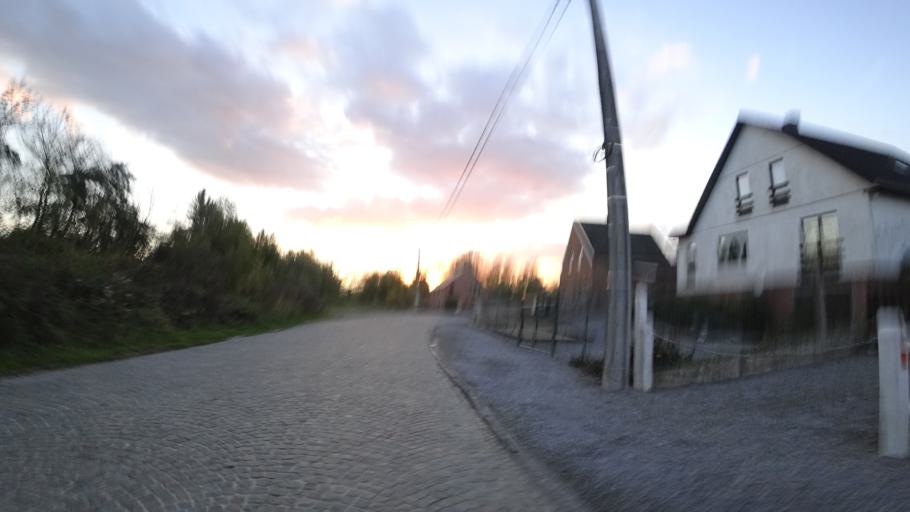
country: BE
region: Wallonia
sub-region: Province de Namur
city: Gembloux
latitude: 50.5541
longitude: 4.7322
